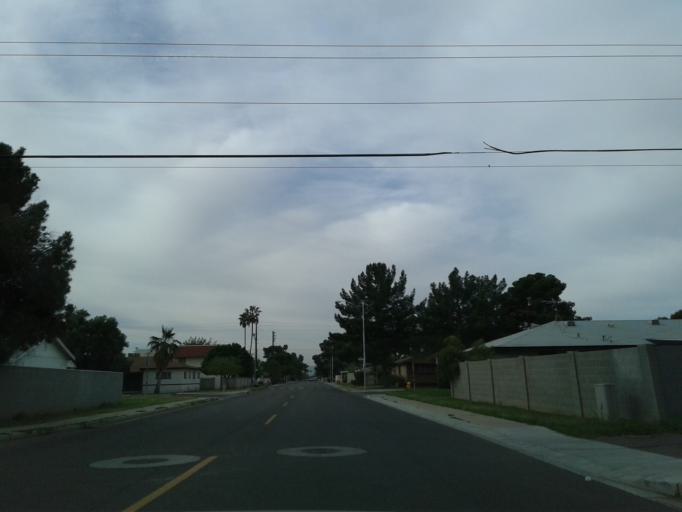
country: US
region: Arizona
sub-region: Maricopa County
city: Glendale
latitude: 33.5280
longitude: -112.1040
